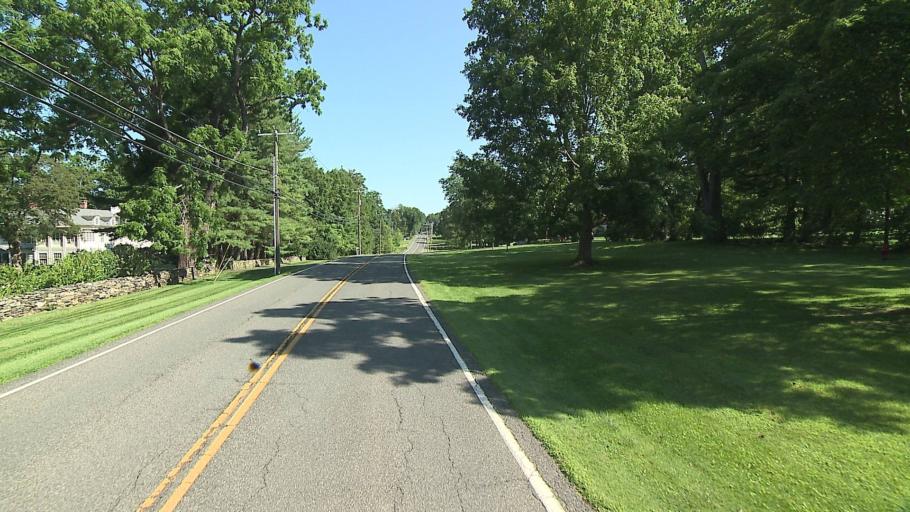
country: US
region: Connecticut
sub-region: Litchfield County
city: Kent
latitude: 41.8726
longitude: -73.4776
